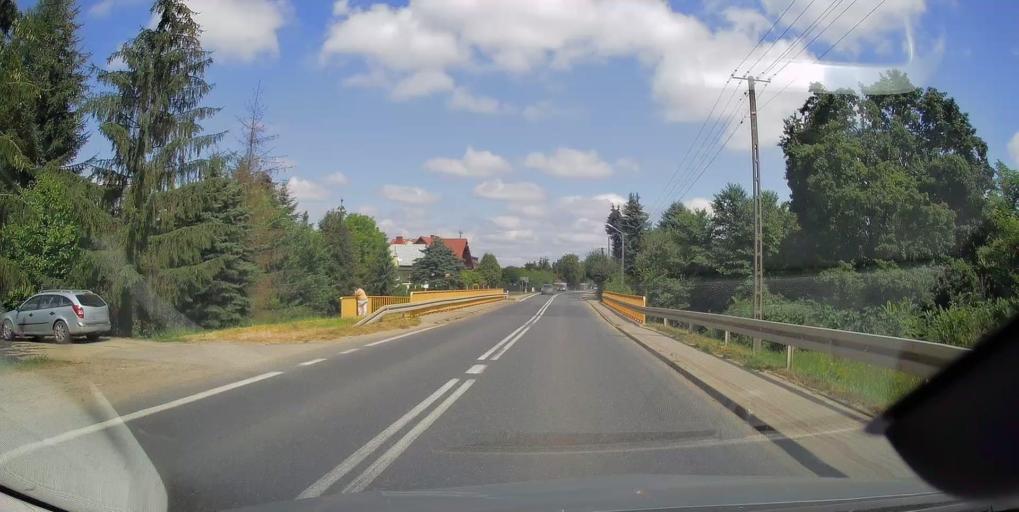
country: PL
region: Subcarpathian Voivodeship
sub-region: Powiat mielecki
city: Przeclaw
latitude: 50.1687
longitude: 21.4894
